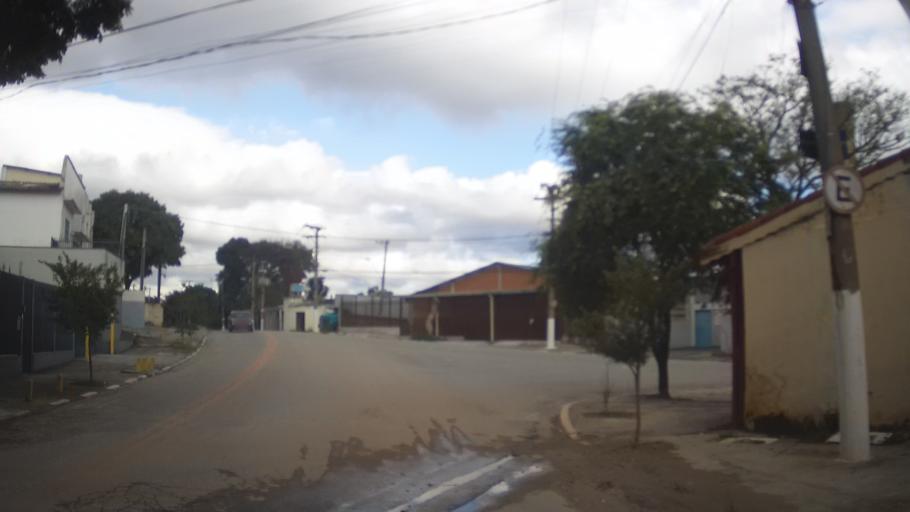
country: BR
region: Sao Paulo
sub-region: Guarulhos
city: Guarulhos
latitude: -23.4639
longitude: -46.4749
